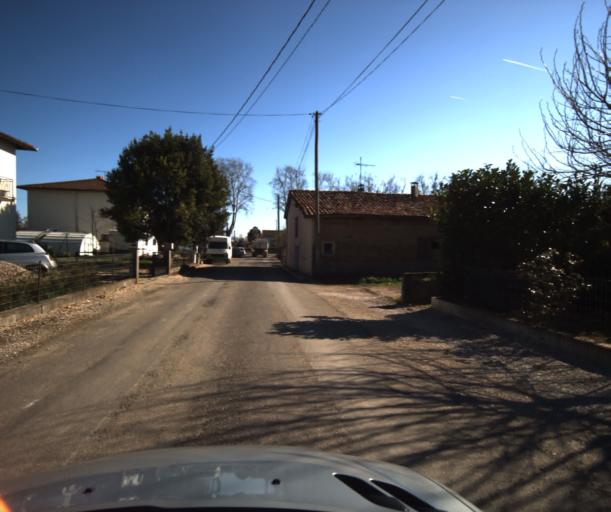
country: FR
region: Midi-Pyrenees
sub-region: Departement du Tarn-et-Garonne
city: Bressols
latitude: 43.9679
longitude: 1.3351
